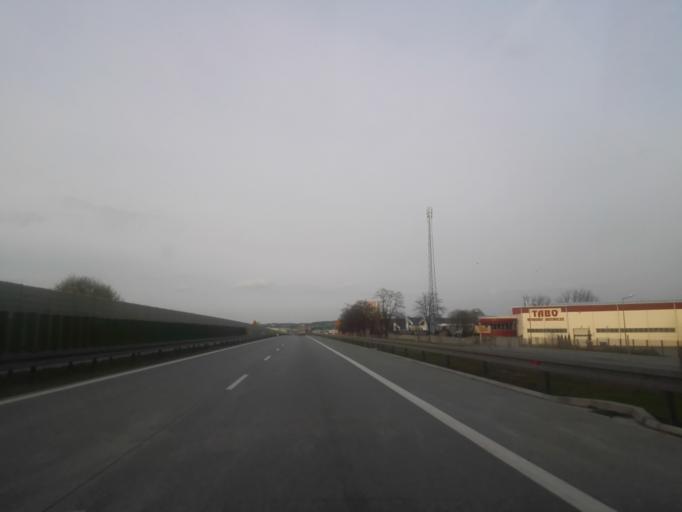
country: PL
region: Lodz Voivodeship
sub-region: Powiat rawski
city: Rawa Mazowiecka
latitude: 51.7571
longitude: 20.2587
